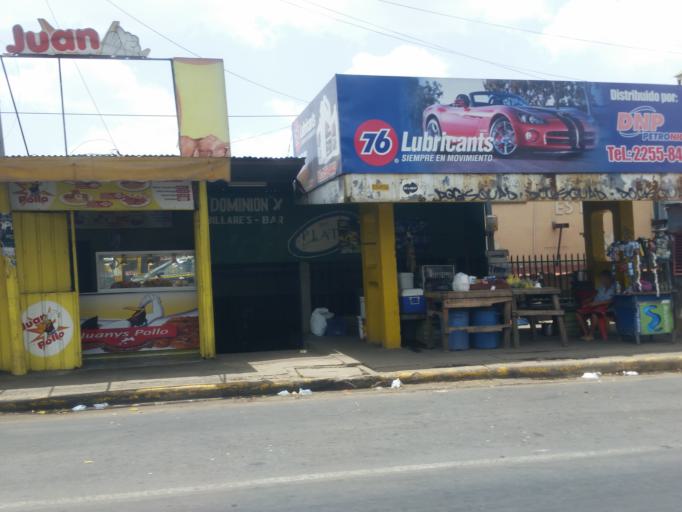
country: NI
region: Managua
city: Managua
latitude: 12.1479
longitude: -86.1938
